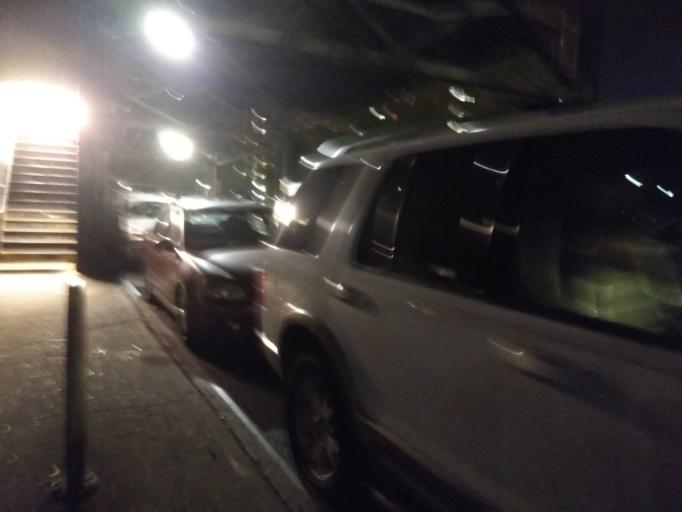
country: US
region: New York
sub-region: Kings County
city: East New York
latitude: 40.6635
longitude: -73.9025
